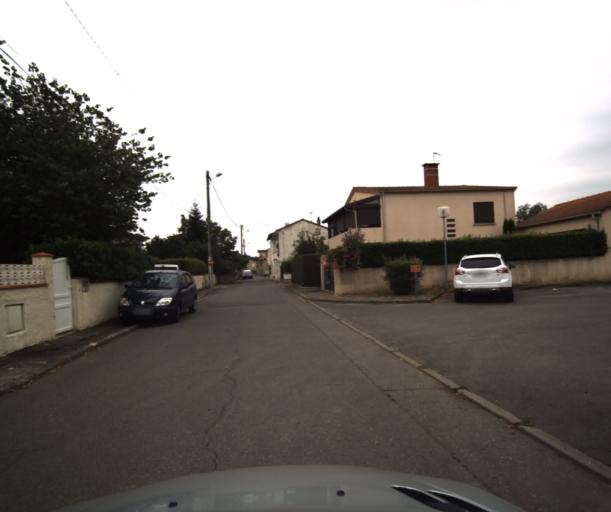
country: FR
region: Midi-Pyrenees
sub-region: Departement de la Haute-Garonne
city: Portet-sur-Garonne
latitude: 43.5257
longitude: 1.4071
